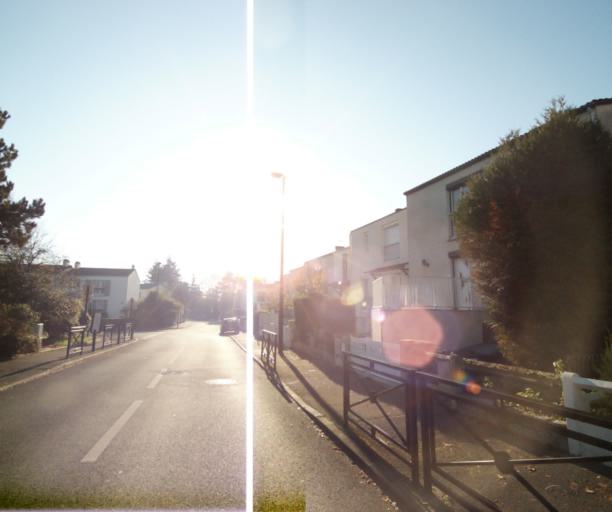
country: FR
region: Ile-de-France
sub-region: Departement du Val-d'Oise
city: Arnouville
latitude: 48.9917
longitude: 2.4245
